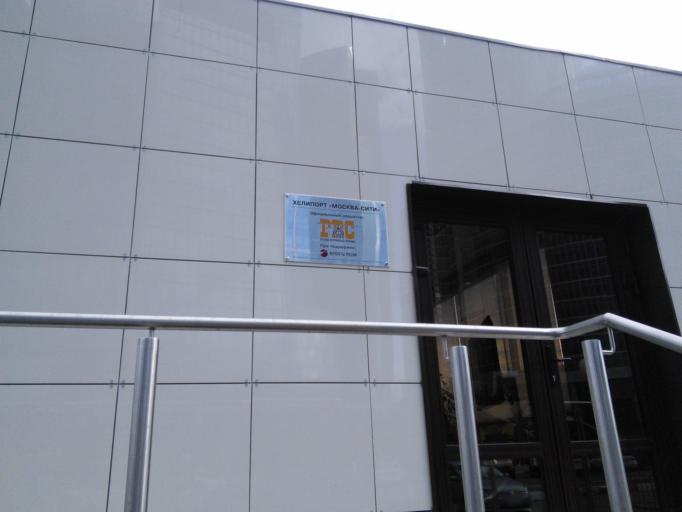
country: RU
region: Moskovskaya
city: Presnenskiy
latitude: 55.7462
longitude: 37.5396
